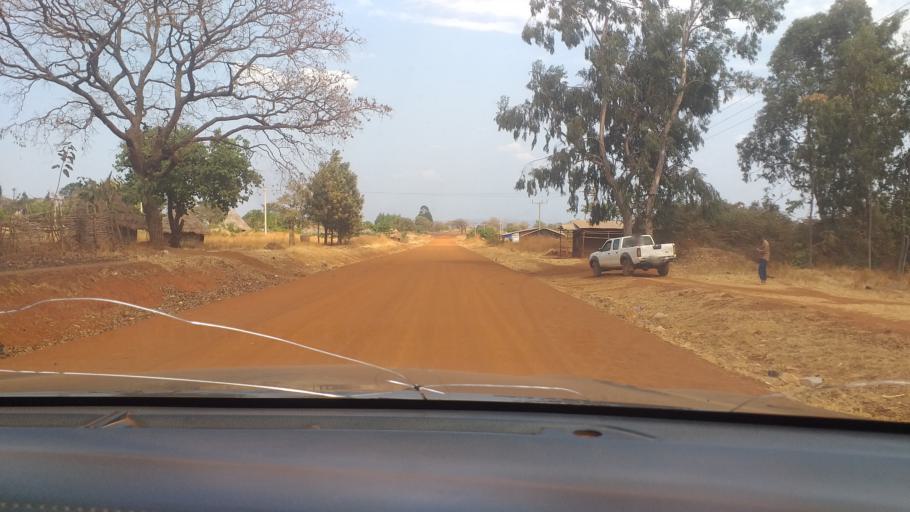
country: ET
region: Binshangul Gumuz
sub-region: Asosa
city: Asosa
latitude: 10.0622
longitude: 34.6954
